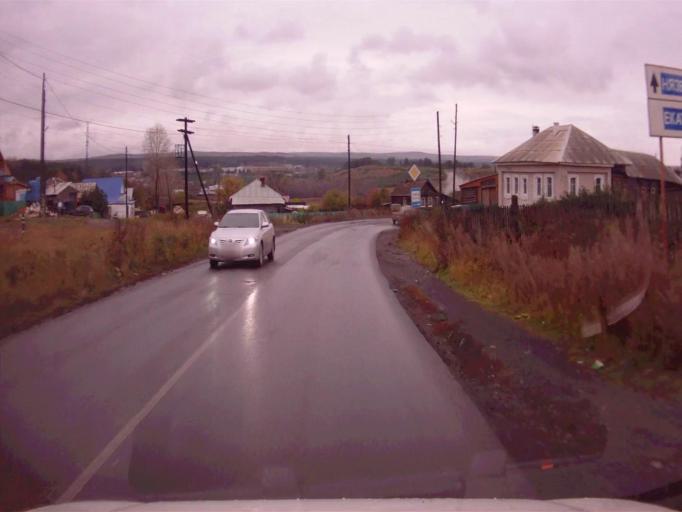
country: RU
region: Chelyabinsk
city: Verkhniy Ufaley
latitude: 56.0588
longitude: 60.2034
